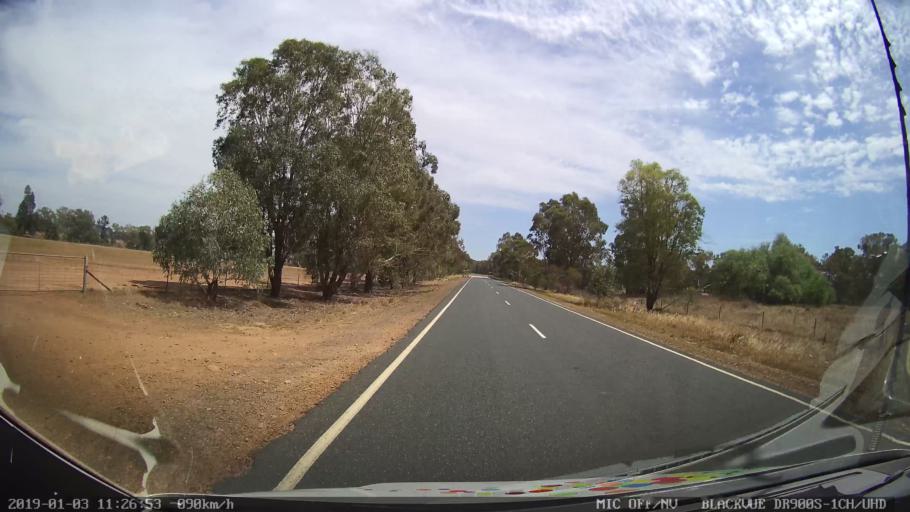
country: AU
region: New South Wales
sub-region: Weddin
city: Grenfell
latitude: -34.0193
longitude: 148.2225
